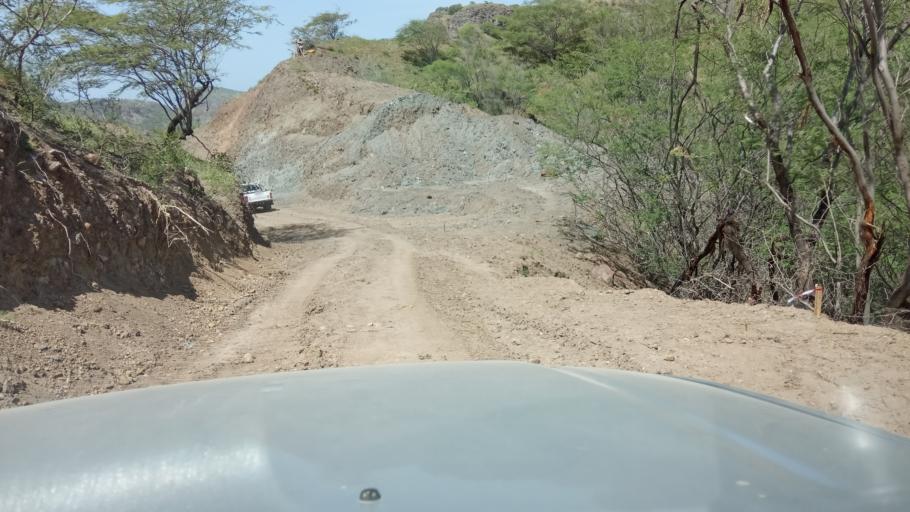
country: CV
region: Santa Catarina
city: Assomada
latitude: 15.1153
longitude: -23.7287
